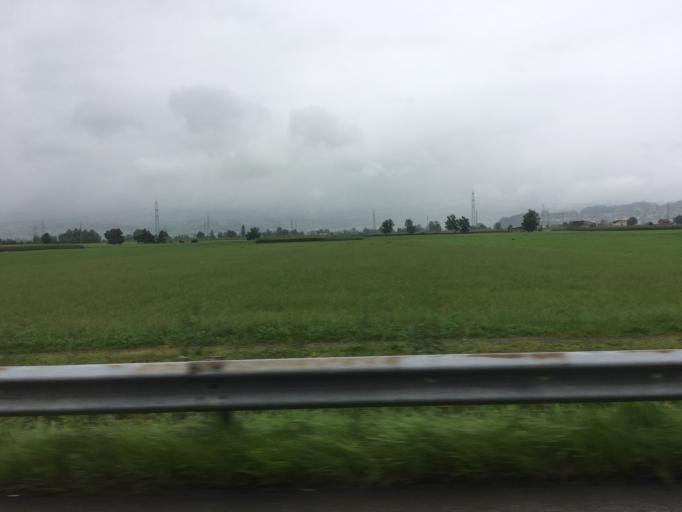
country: CH
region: Schwyz
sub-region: Bezirk March
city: Tuggen
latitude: 47.1979
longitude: 8.9700
